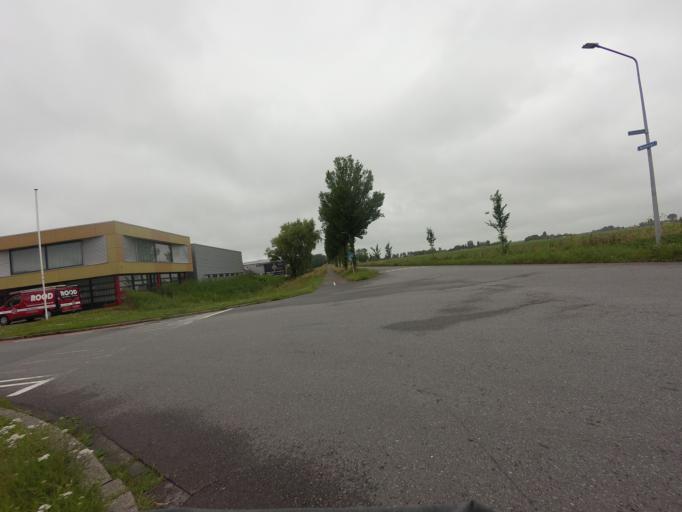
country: NL
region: North Holland
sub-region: Gemeente Opmeer
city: Opmeer
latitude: 52.7620
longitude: 4.8930
